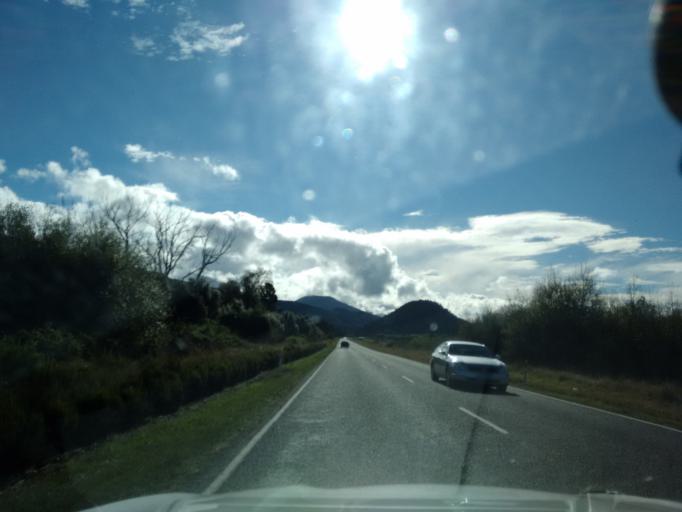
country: NZ
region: Waikato
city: Turangi
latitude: -38.9881
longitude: 175.7896
